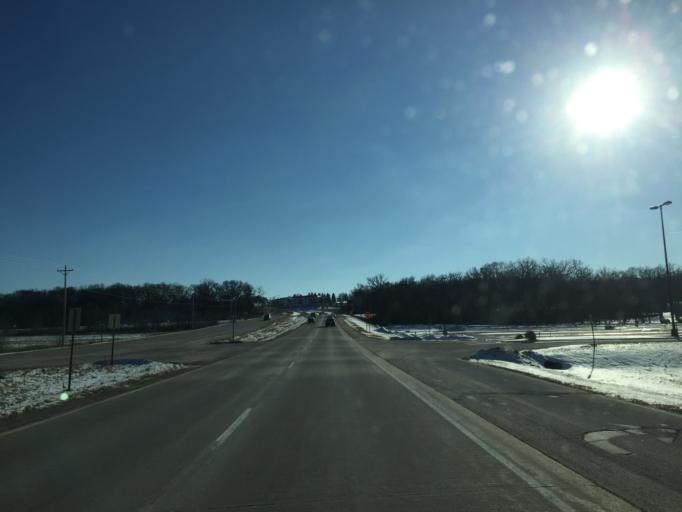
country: US
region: Minnesota
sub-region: Olmsted County
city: Rochester
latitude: 44.0152
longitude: -92.4194
